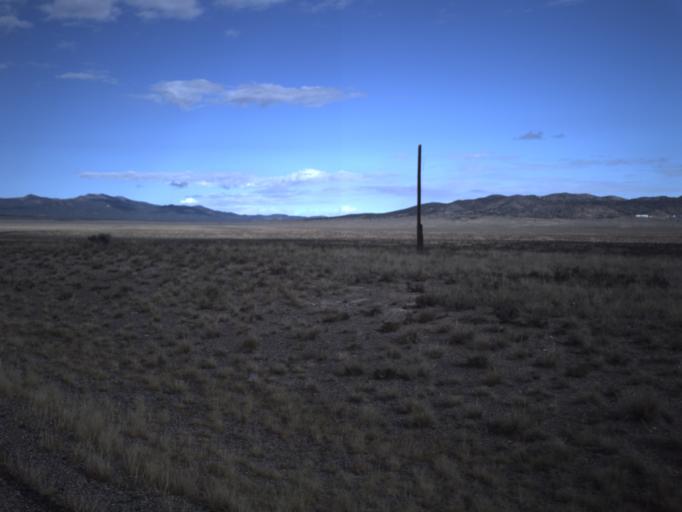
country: US
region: Utah
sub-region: Beaver County
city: Milford
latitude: 38.4326
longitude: -113.1314
